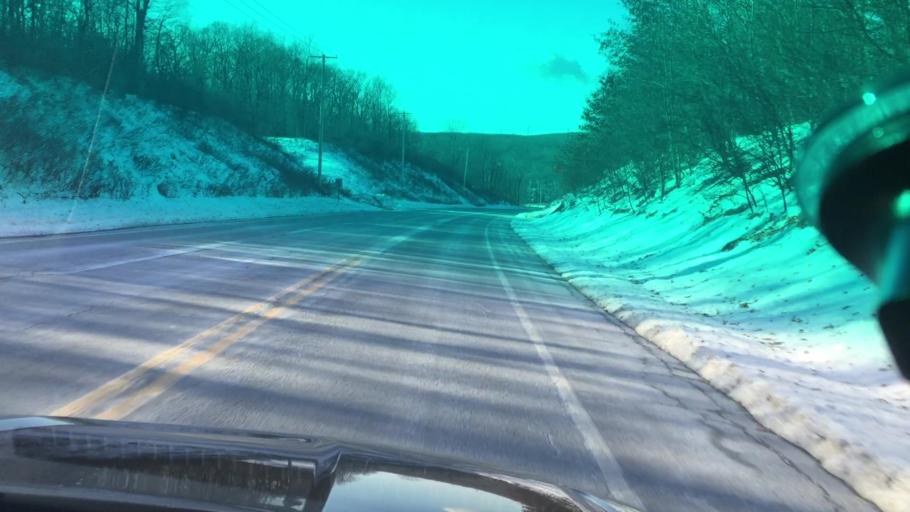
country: US
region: Pennsylvania
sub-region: Luzerne County
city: Oakdale
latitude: 41.0177
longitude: -75.9268
